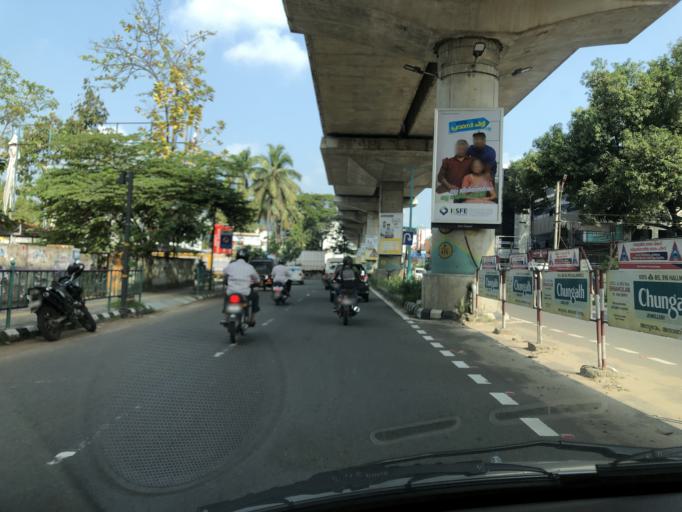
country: IN
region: Kerala
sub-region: Ernakulam
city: Elur
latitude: 10.0127
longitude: 76.3030
